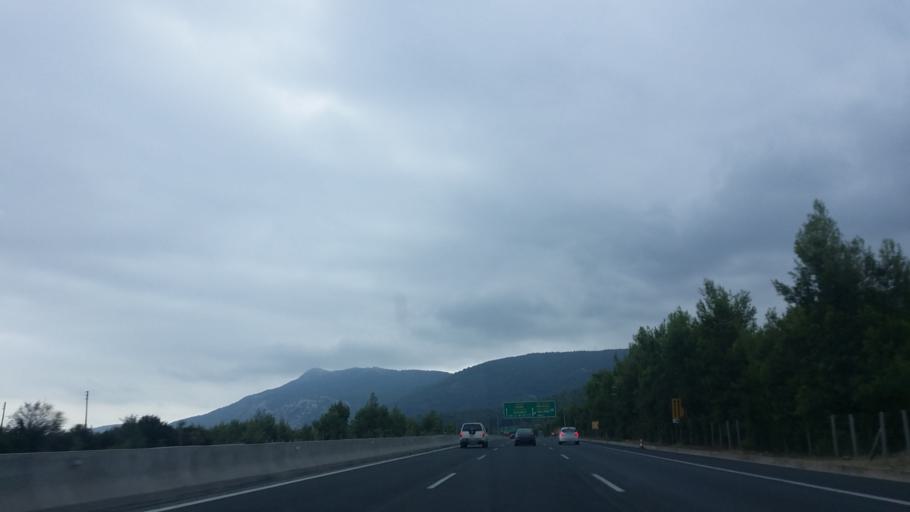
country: GR
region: Attica
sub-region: Nomarchia Anatolikis Attikis
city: Oropos
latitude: 38.2450
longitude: 23.7691
